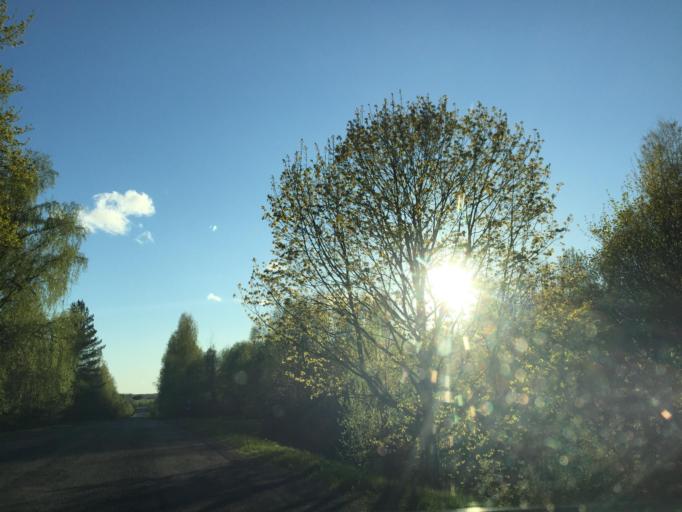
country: LV
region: Ergli
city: Ergli
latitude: 56.8687
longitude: 25.7859
